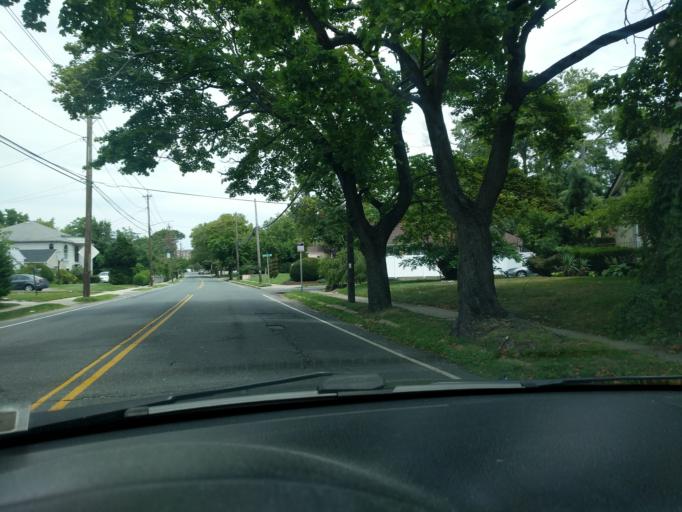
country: US
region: New York
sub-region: Nassau County
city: Woodmere
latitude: 40.6300
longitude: -73.7178
